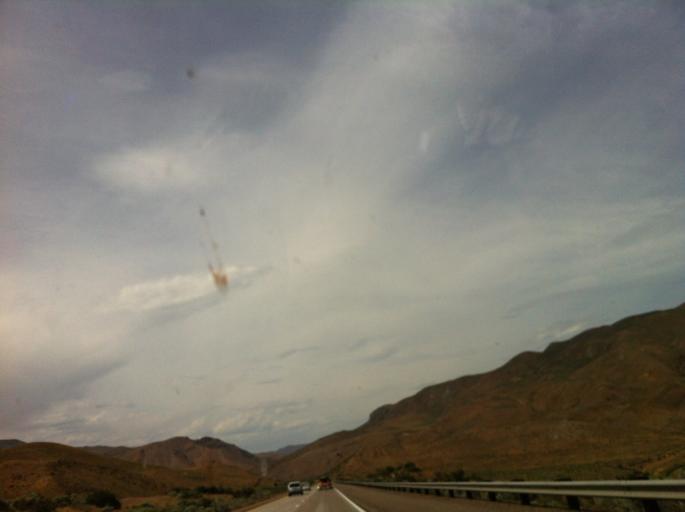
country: US
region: Idaho
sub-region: Washington County
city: Weiser
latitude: 44.3590
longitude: -117.2919
